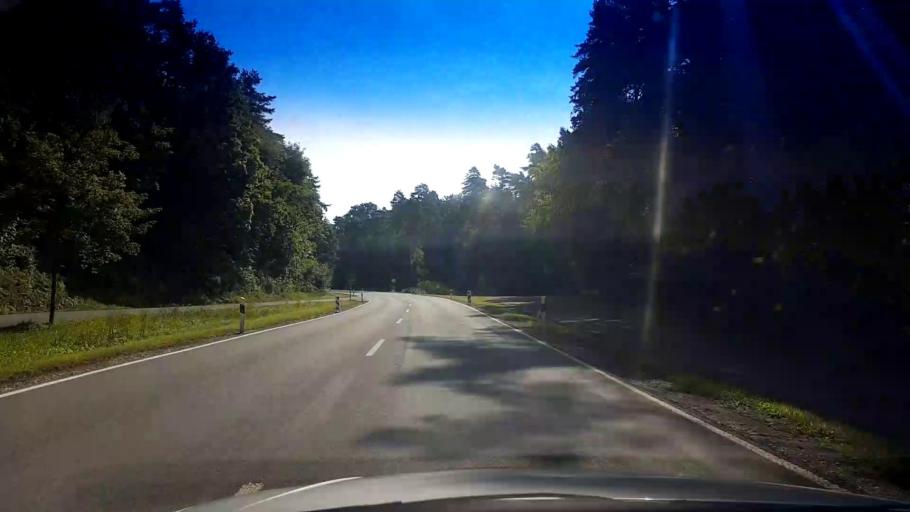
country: DE
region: Bavaria
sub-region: Upper Franconia
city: Hollfeld
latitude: 49.9388
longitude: 11.2998
